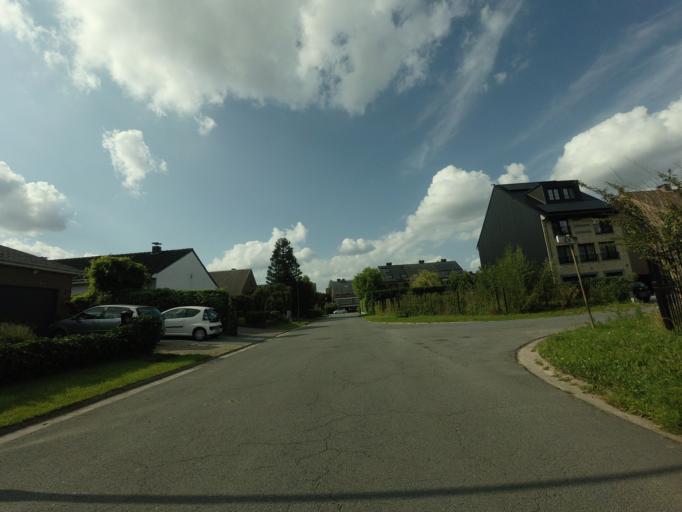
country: BE
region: Flanders
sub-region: Provincie Vlaams-Brabant
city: Meise
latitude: 50.9258
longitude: 4.3395
